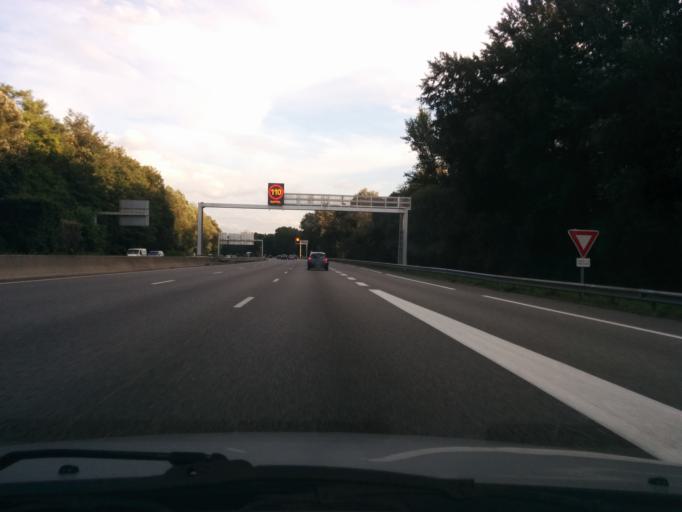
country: FR
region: Rhone-Alpes
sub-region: Departement de l'Isere
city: Veurey-Voroize
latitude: 45.2701
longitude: 5.6270
